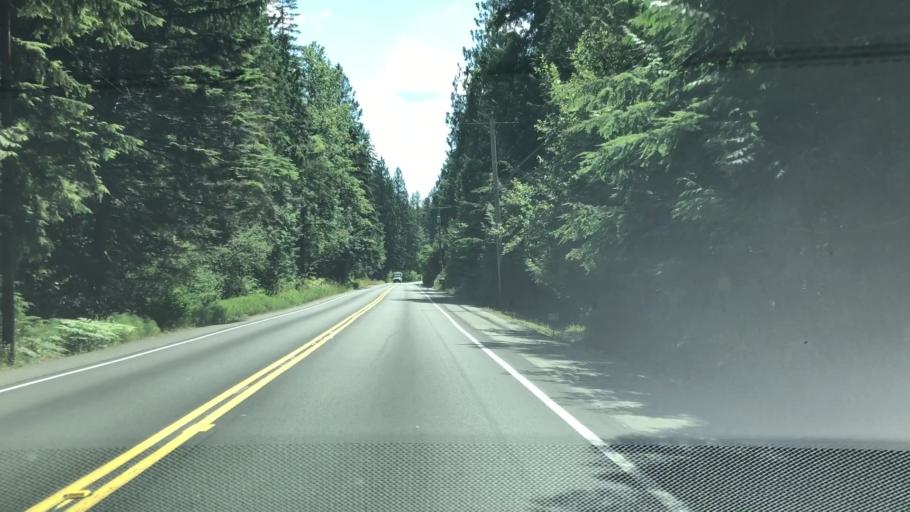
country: US
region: Washington
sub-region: King County
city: Cottage Lake
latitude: 47.7528
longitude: -122.0620
